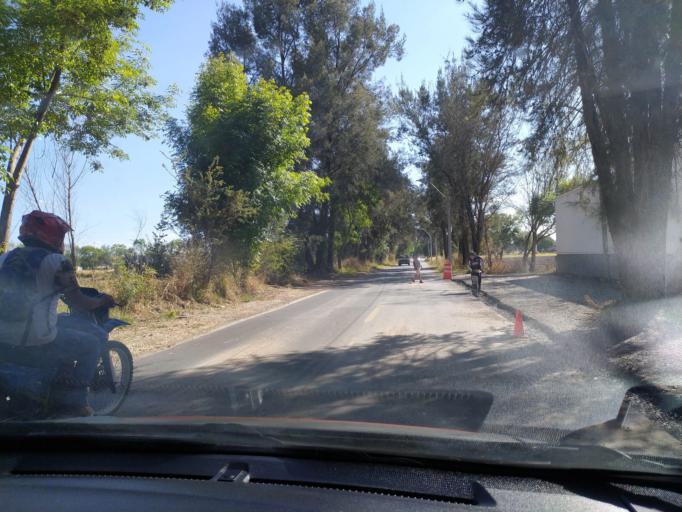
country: LA
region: Oudomxai
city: Muang La
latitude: 21.0423
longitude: 101.8372
